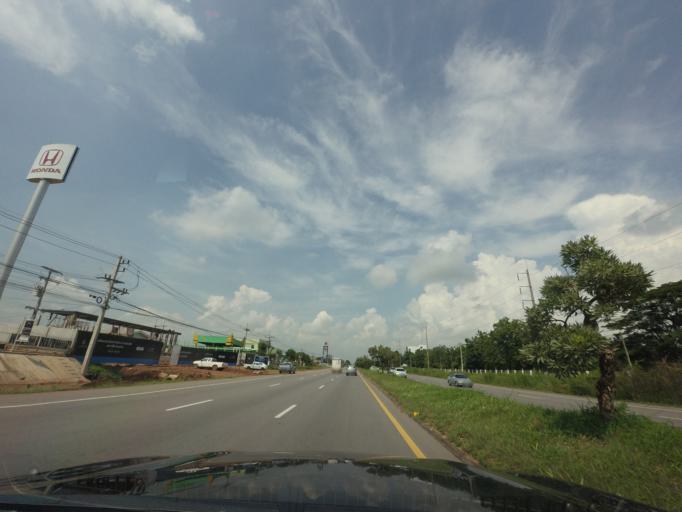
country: TH
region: Khon Kaen
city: Khon Kaen
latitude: 16.4506
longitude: 102.7412
